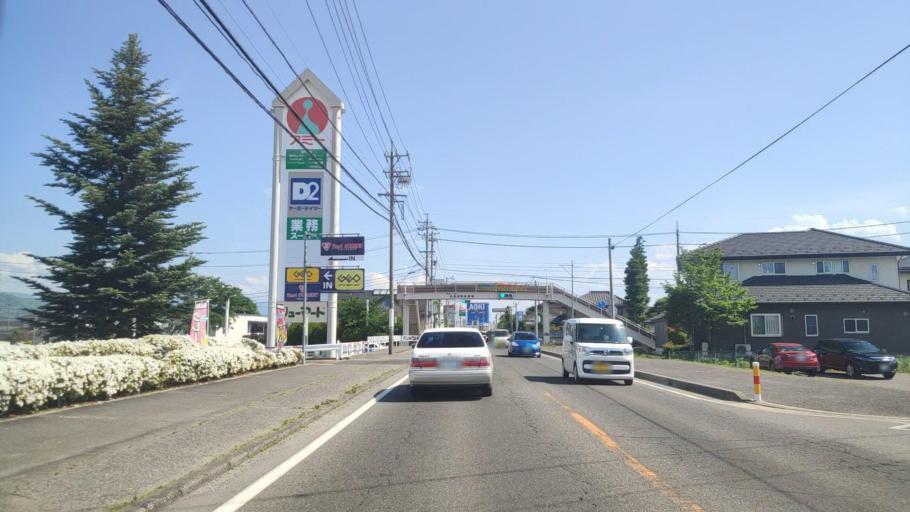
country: JP
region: Nagano
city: Hotaka
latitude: 36.3342
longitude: 137.8904
